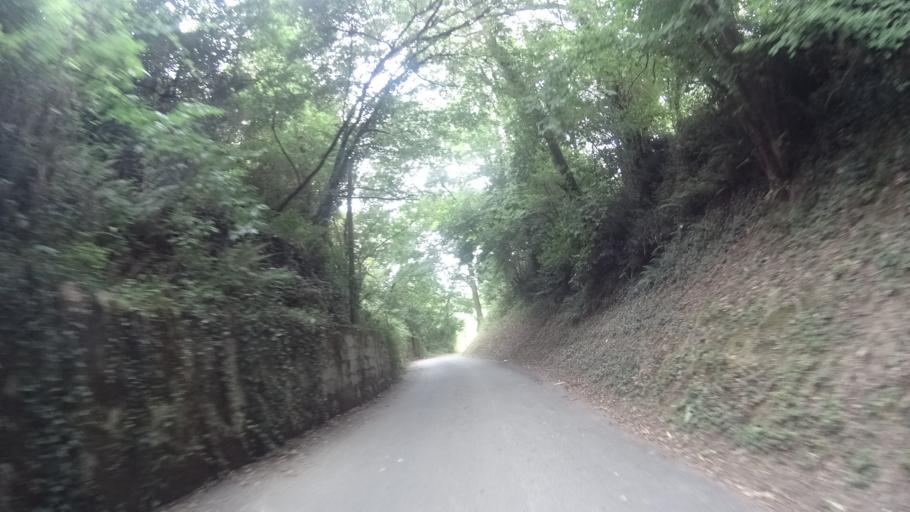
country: FR
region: Aquitaine
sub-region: Departement des Pyrenees-Atlantiques
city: Orthez
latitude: 43.4680
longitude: -0.7162
